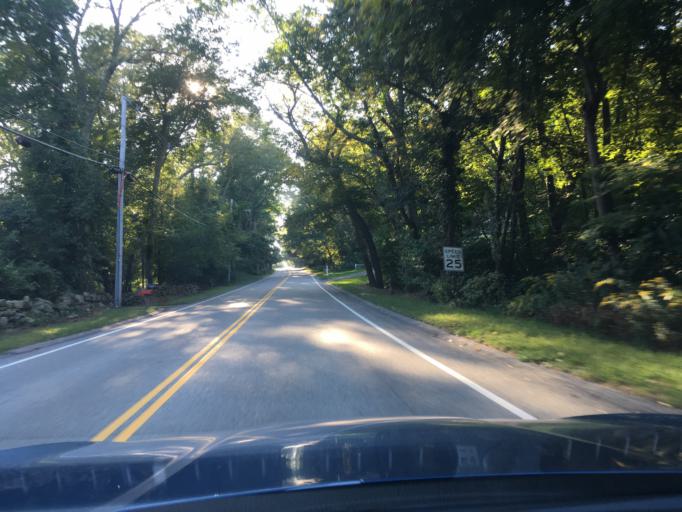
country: US
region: Rhode Island
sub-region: Kent County
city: East Greenwich
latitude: 41.6453
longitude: -71.4967
